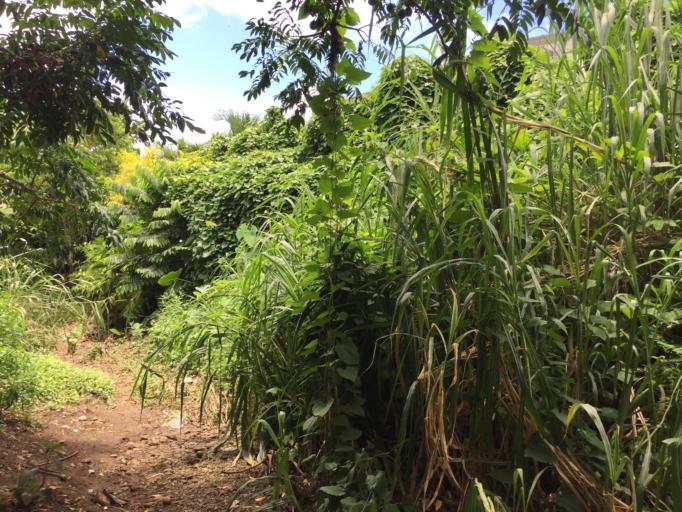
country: WS
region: Tuamasaga
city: Apia
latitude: -13.8564
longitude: -171.7830
